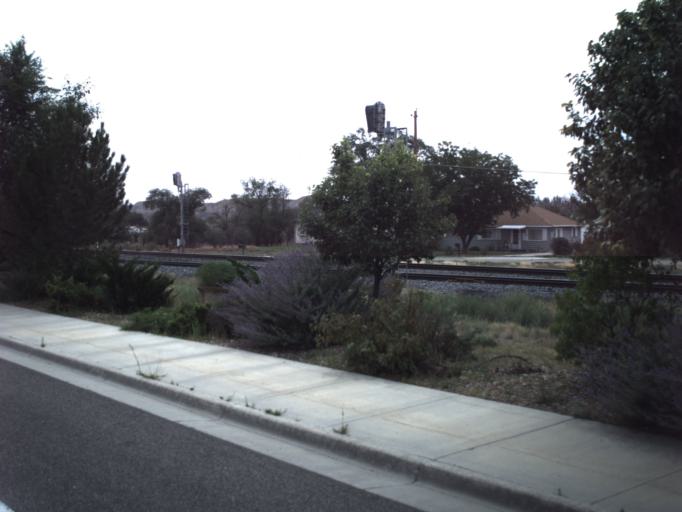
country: US
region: Utah
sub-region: Carbon County
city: Wellington
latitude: 39.5430
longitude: -110.7406
